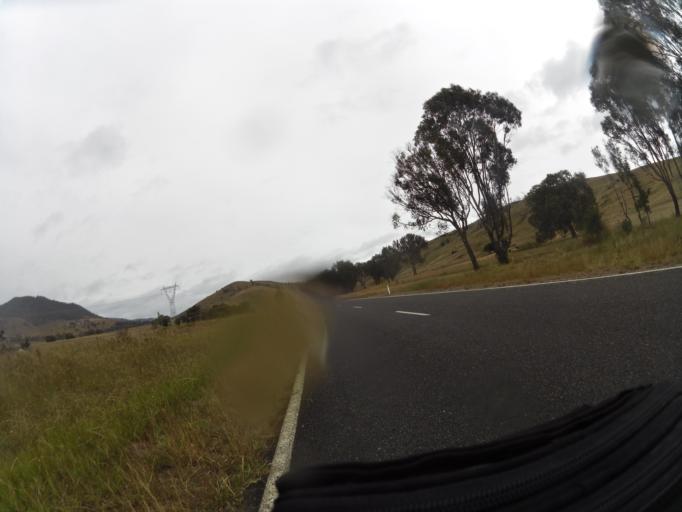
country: AU
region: New South Wales
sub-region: Greater Hume Shire
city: Holbrook
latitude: -36.2079
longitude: 147.7358
